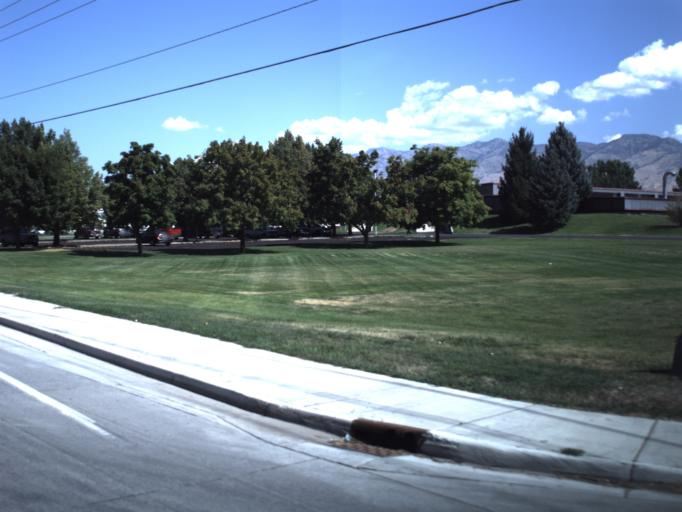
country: US
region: Utah
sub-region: Cache County
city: Logan
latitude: 41.7414
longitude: -111.8593
